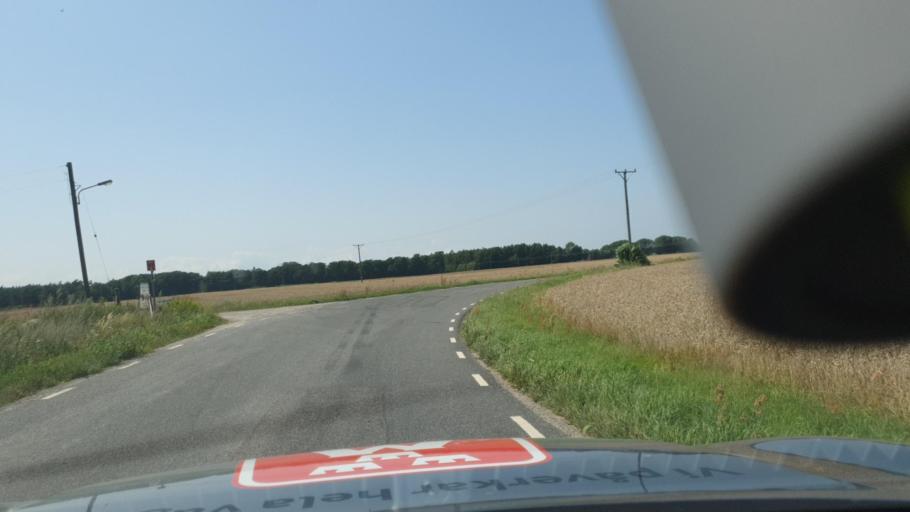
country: SE
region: Skane
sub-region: Bromolla Kommun
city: Bromoella
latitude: 56.0467
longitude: 14.3962
